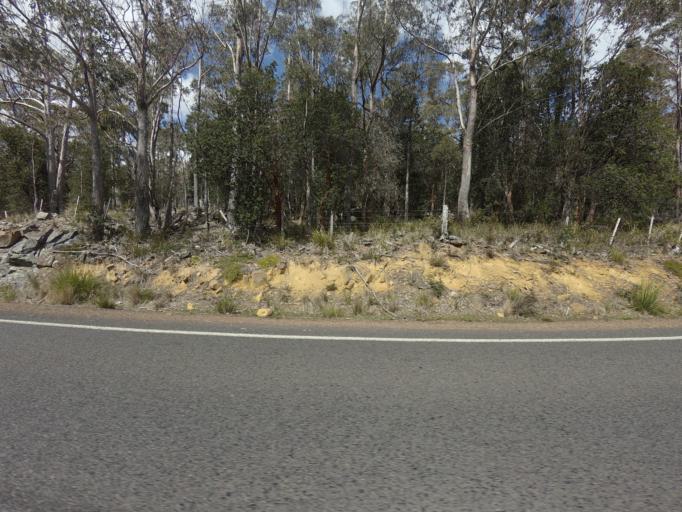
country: AU
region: Tasmania
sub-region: Northern Midlands
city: Evandale
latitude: -42.0047
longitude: 147.7230
